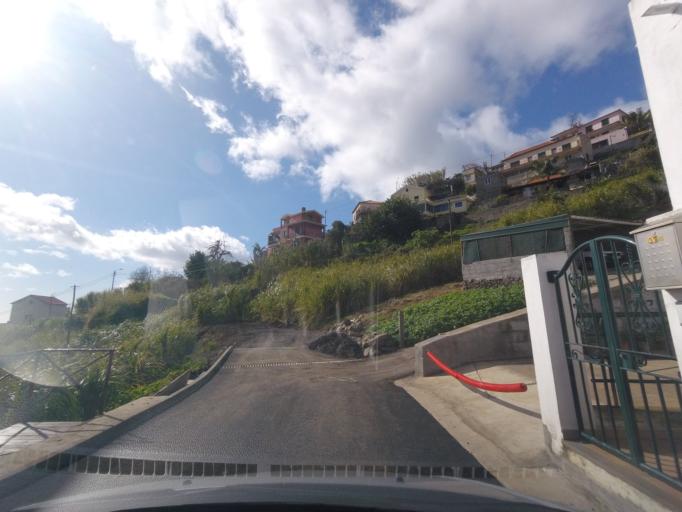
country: PT
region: Madeira
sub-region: Ribeira Brava
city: Campanario
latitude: 32.6641
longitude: -17.0224
